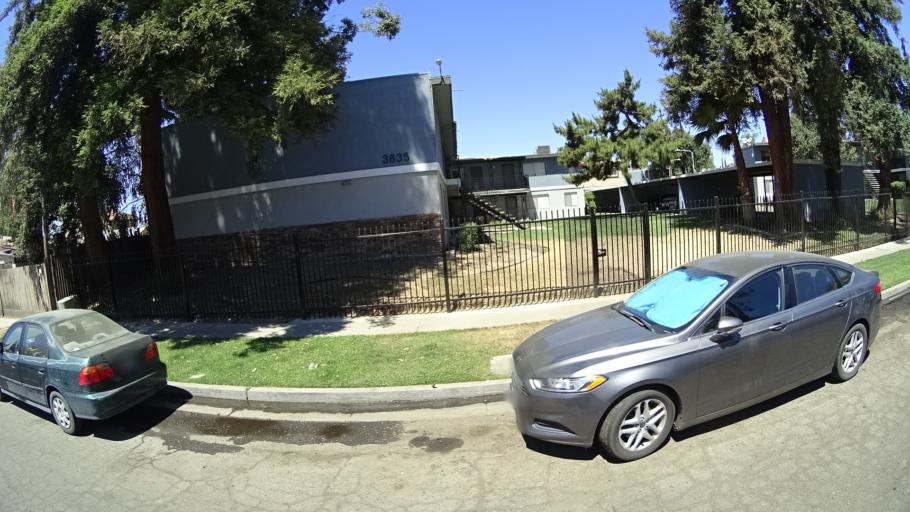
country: US
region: California
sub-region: Fresno County
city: Fresno
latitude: 36.7873
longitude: -119.8131
